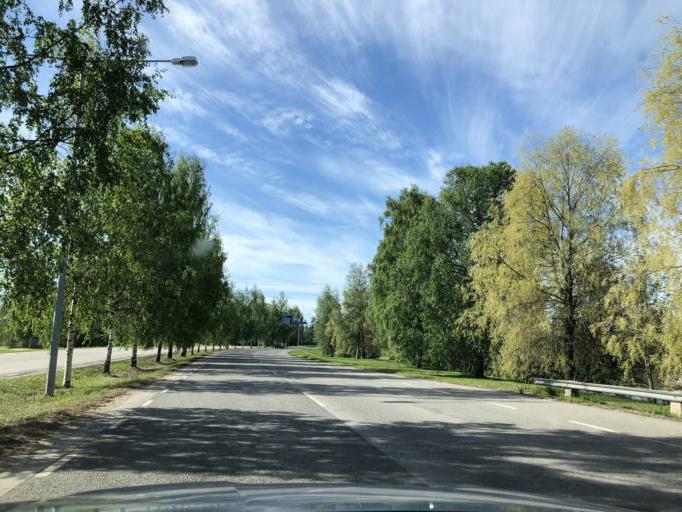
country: SE
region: Norrbotten
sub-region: Pitea Kommun
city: Pitea
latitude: 65.3135
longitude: 21.4918
